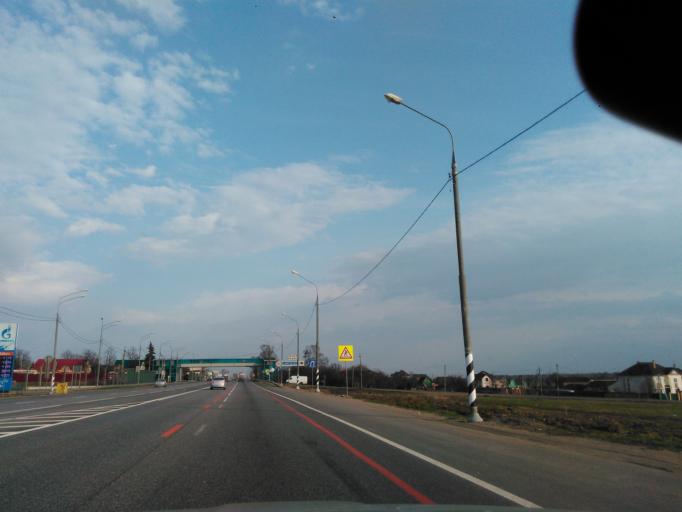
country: RU
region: Moskovskaya
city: Peshki
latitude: 56.1339
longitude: 37.0624
